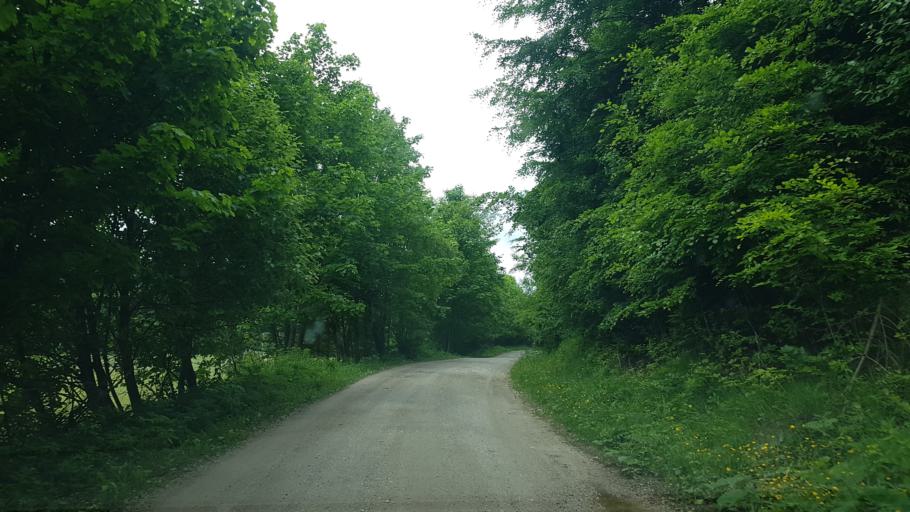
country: SI
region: Dobrna
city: Dobrna
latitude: 46.3829
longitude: 15.2321
